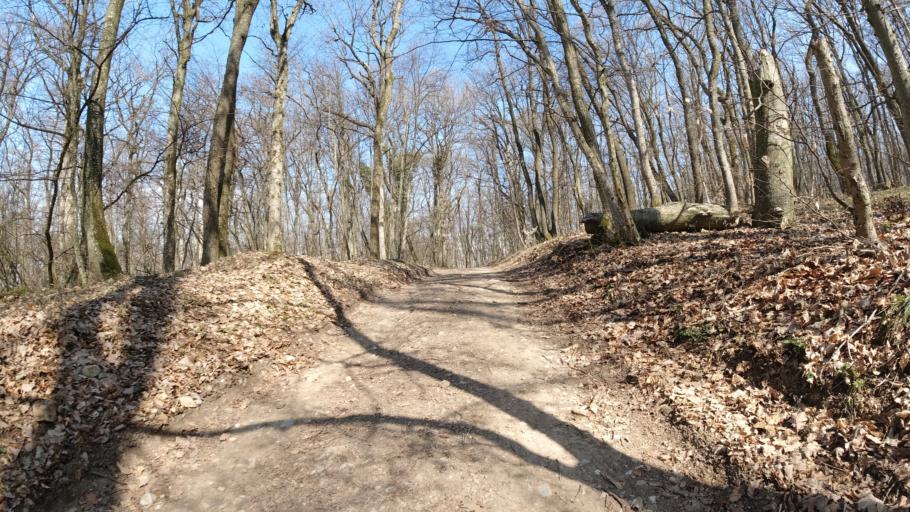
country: SK
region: Trnavsky
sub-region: Okres Trnava
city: Piestany
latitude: 48.5701
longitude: 17.8835
